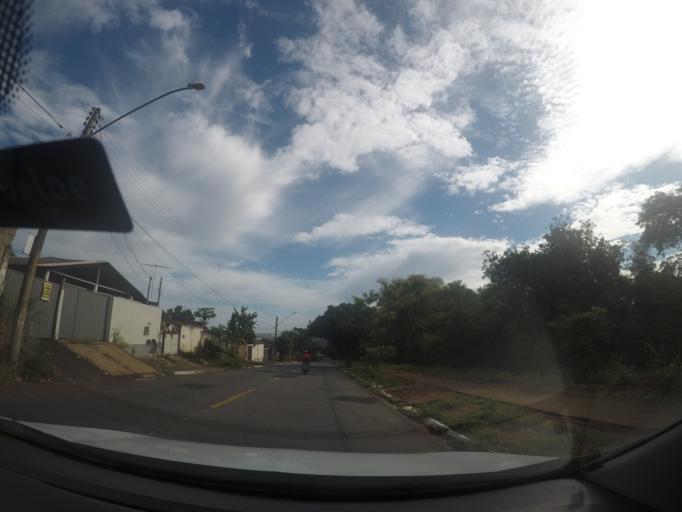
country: BR
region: Goias
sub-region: Goiania
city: Goiania
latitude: -16.6894
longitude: -49.2036
